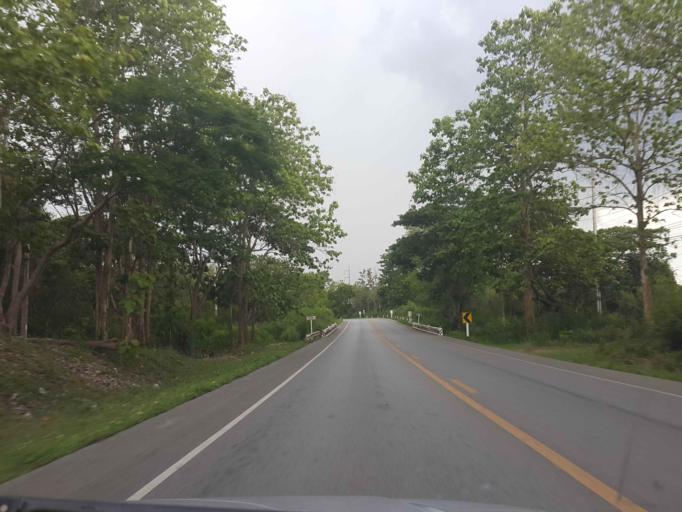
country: TH
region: Phrae
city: Den Chai
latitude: 17.9759
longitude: 100.0389
